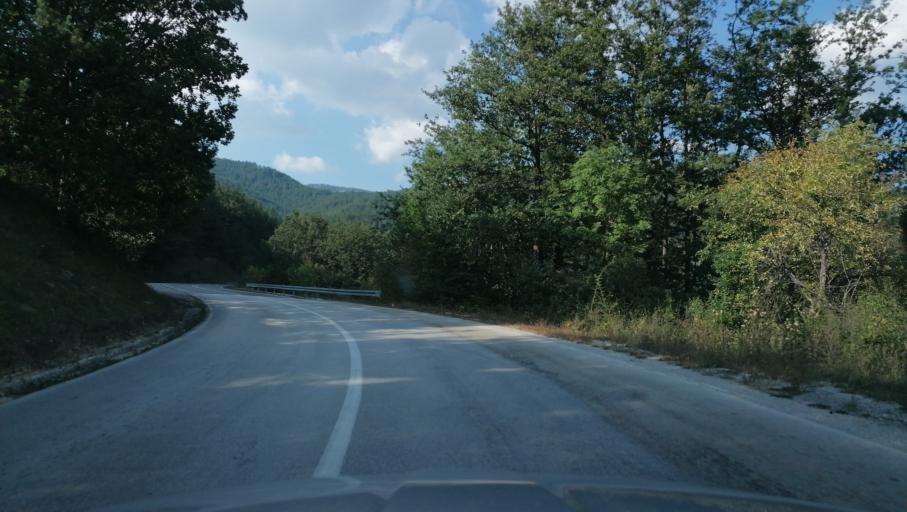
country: RS
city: Durici
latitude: 43.8048
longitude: 19.5117
